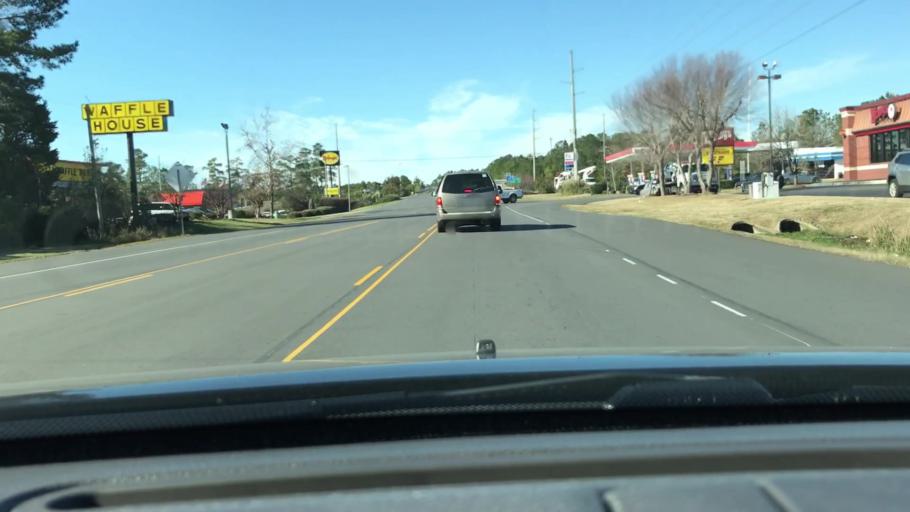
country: US
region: North Carolina
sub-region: Brunswick County
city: Shallotte
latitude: 33.9740
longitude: -78.4009
